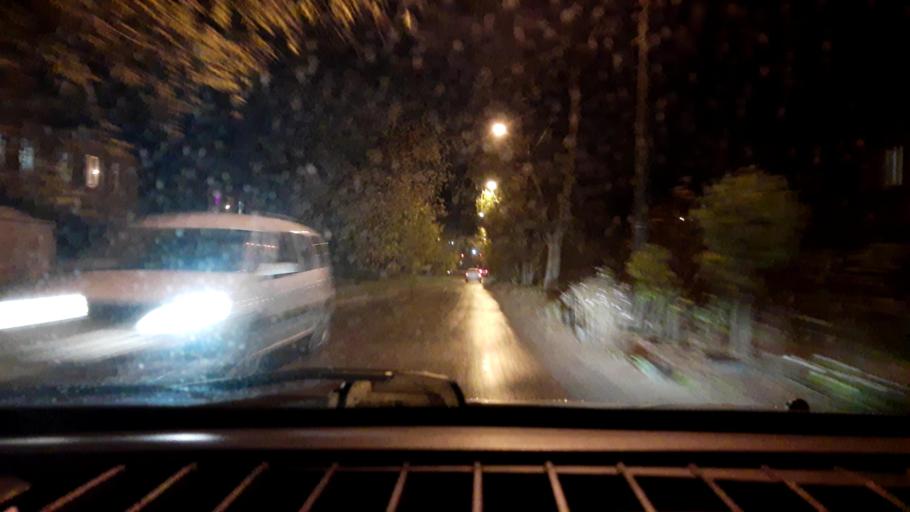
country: RU
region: Nizjnij Novgorod
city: Gorbatovka
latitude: 56.3803
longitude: 43.7923
